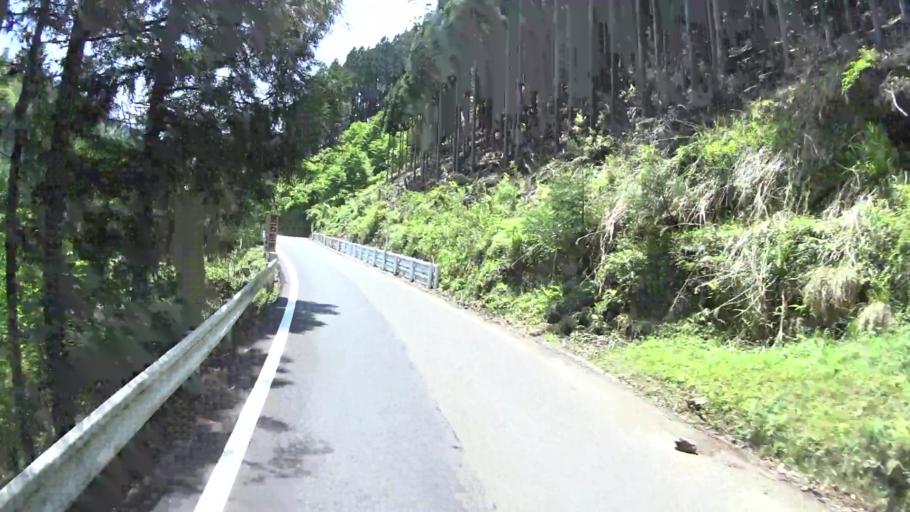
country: JP
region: Kyoto
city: Kameoka
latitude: 35.1220
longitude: 135.5873
